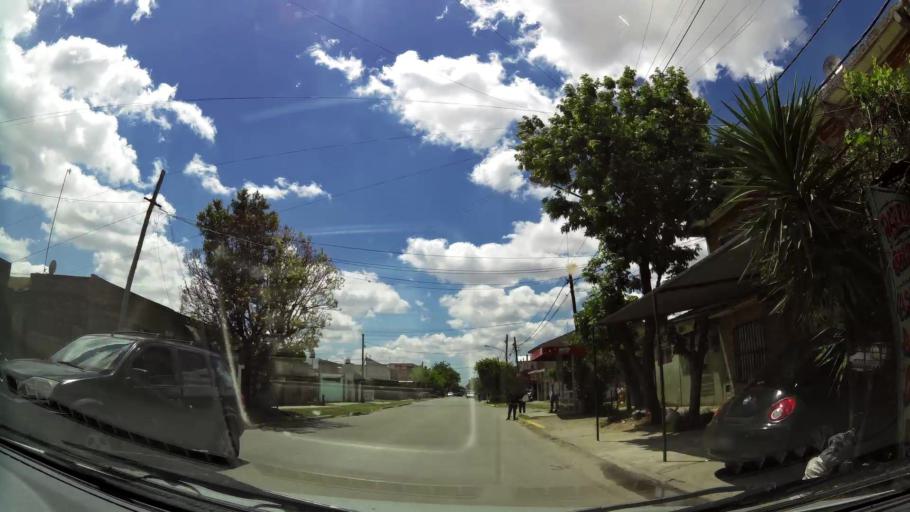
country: AR
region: Buenos Aires
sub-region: Partido de Lanus
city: Lanus
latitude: -34.7005
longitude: -58.4350
